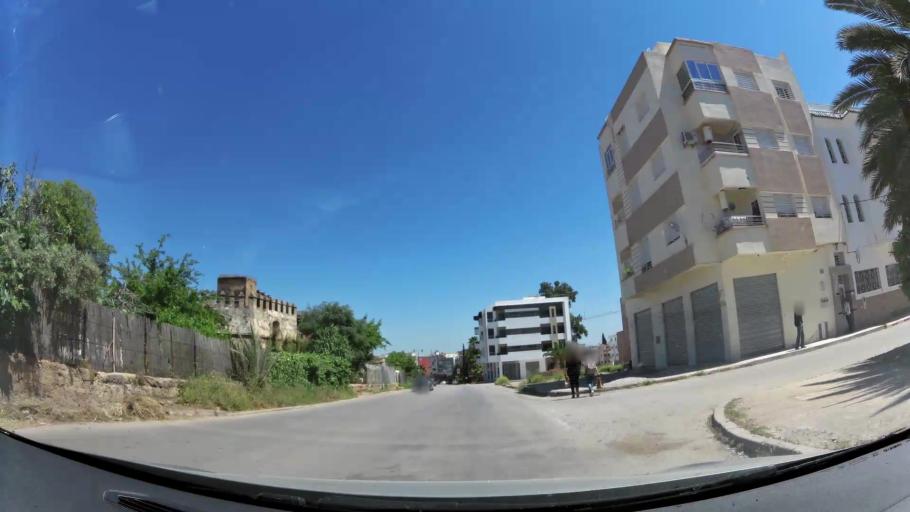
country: MA
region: Fes-Boulemane
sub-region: Fes
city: Fes
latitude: 34.0271
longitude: -5.0014
